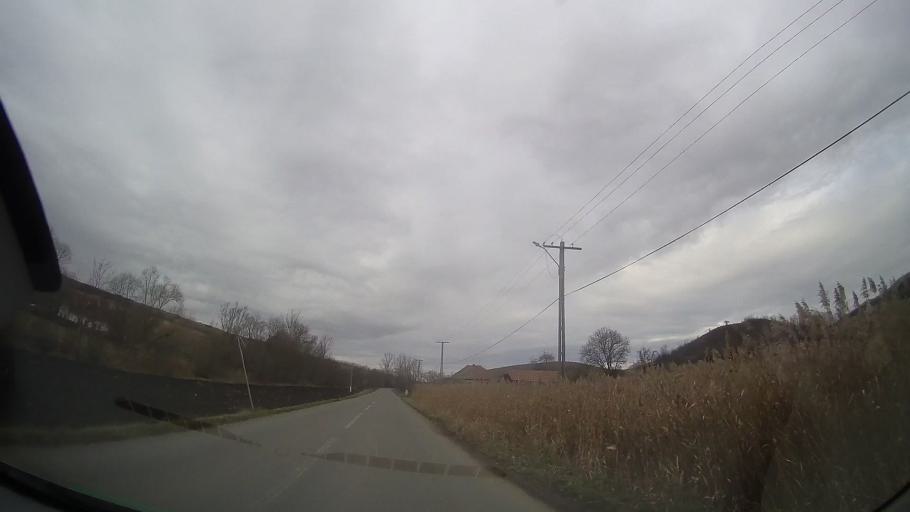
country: RO
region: Mures
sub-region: Comuna Faragau
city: Faragau
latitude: 46.7353
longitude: 24.5437
